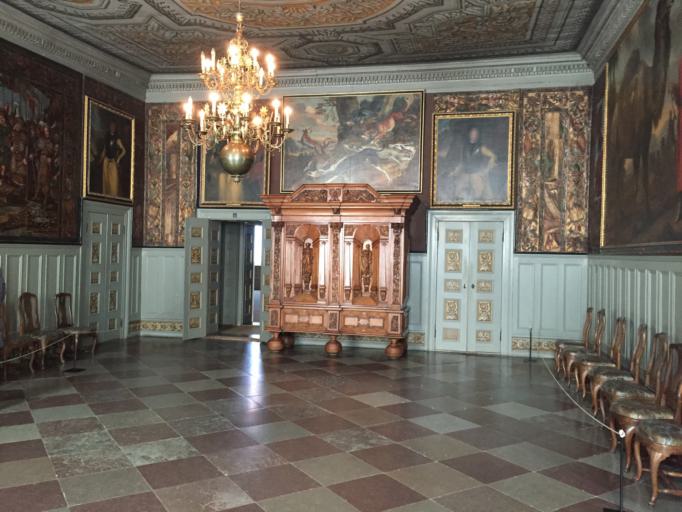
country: SE
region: Stockholm
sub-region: Stockholms Kommun
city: Bromma
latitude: 59.3218
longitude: 17.8869
